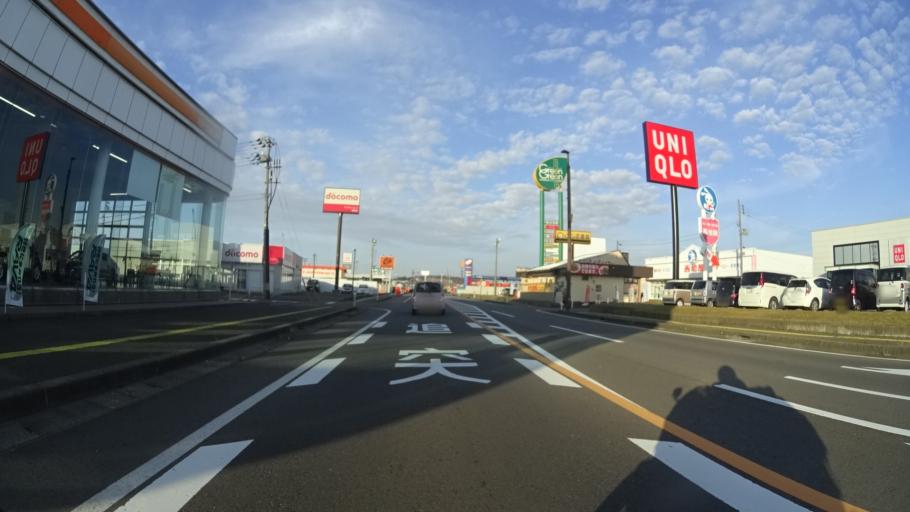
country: JP
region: Niigata
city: Kashiwazaki
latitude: 37.3782
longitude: 138.5804
